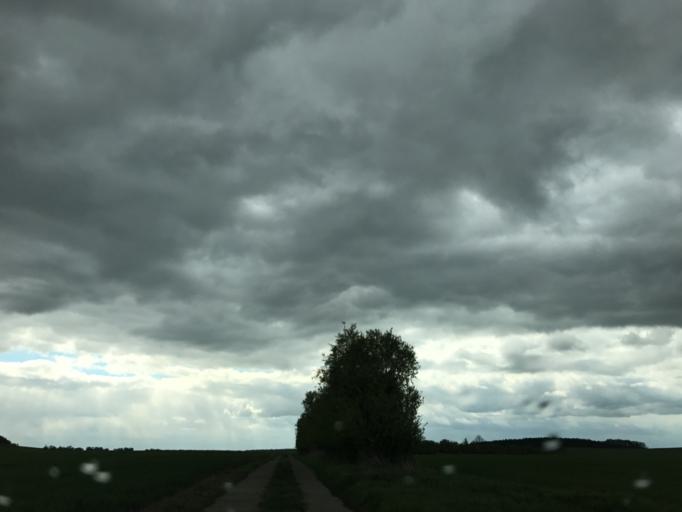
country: DE
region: Brandenburg
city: Roskow
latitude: 52.4993
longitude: 12.7714
